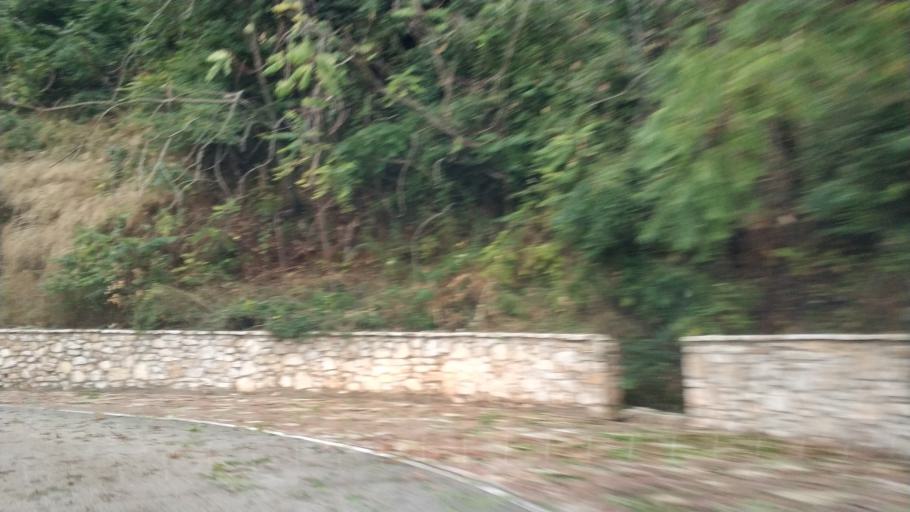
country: AL
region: Vlore
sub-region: Rrethi i Sarandes
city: Lukove
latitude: 39.9464
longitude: 19.9679
